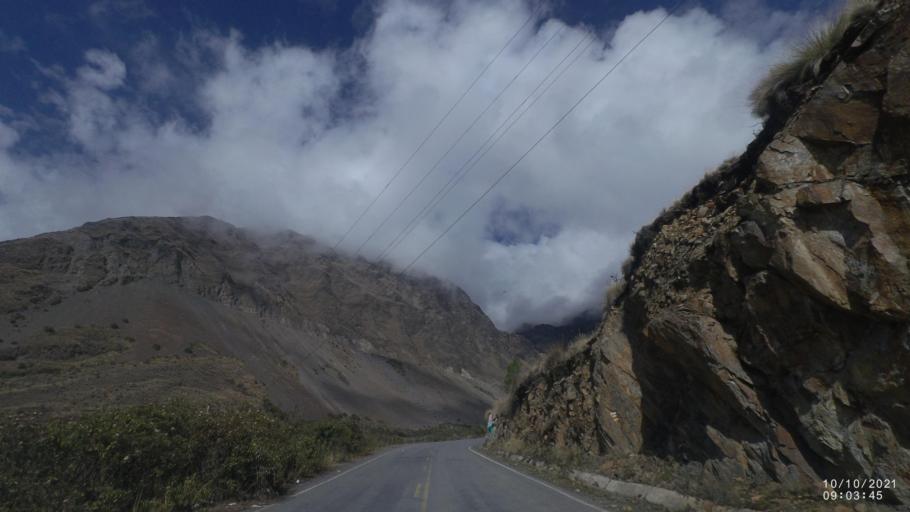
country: BO
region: La Paz
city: Quime
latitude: -17.0023
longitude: -67.2717
